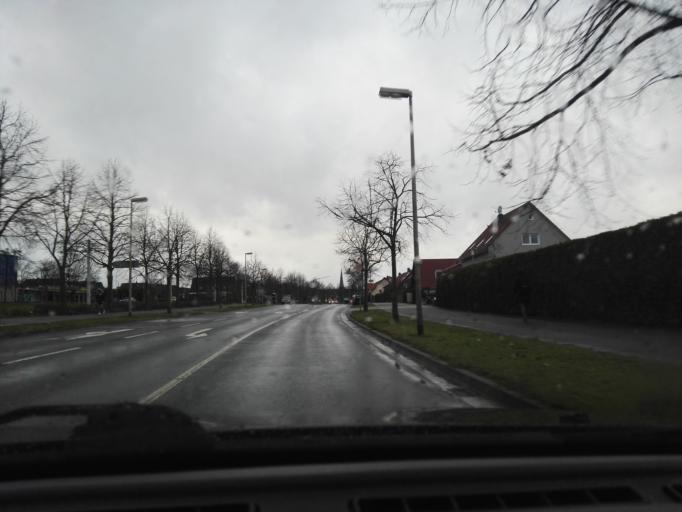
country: DE
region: Lower Saxony
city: Leiferde
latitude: 52.2340
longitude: 10.4867
